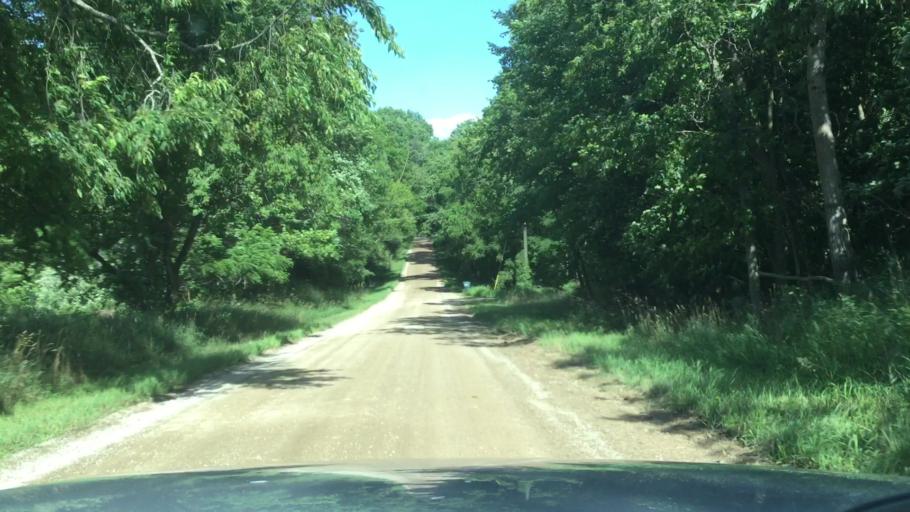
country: US
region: Michigan
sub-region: Ionia County
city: Belding
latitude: 43.0745
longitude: -85.2239
